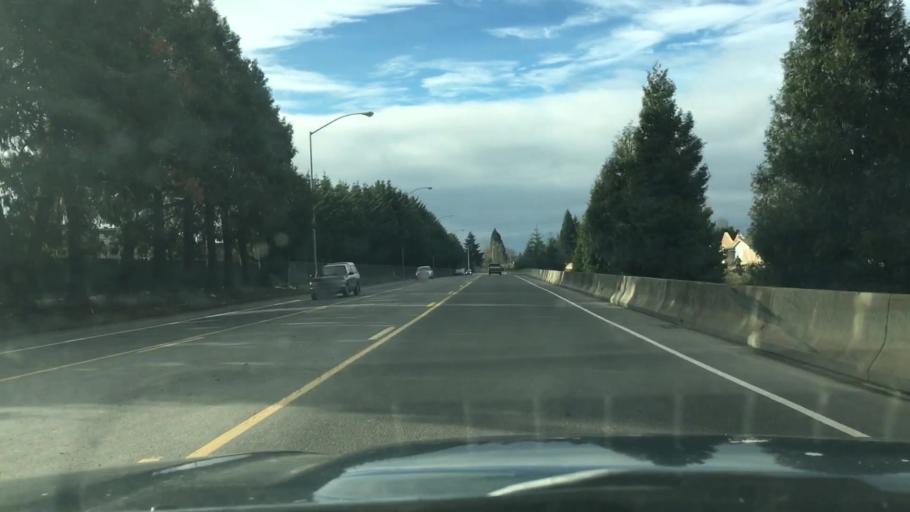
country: US
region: Oregon
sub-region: Lane County
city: Eugene
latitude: 44.0633
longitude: -123.1524
